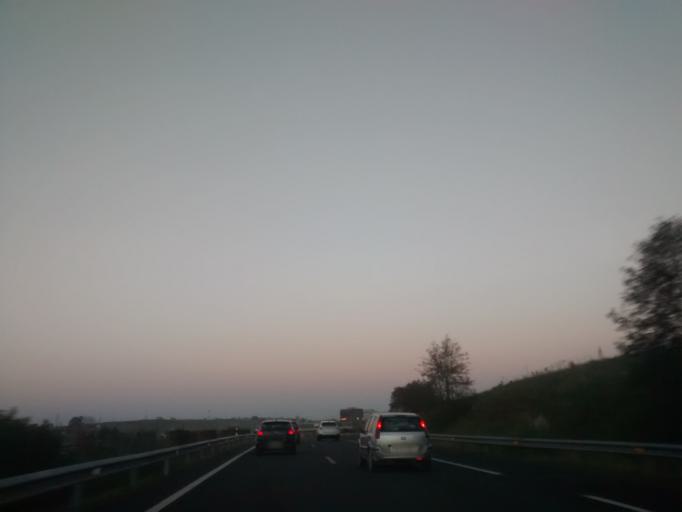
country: ES
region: Cantabria
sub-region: Provincia de Cantabria
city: Santa Cruz de Bezana
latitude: 43.4464
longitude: -3.8862
